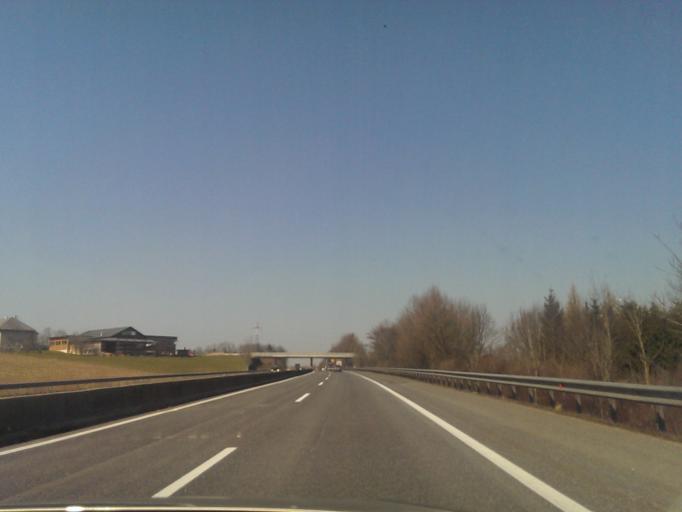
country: AT
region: Upper Austria
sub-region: Politischer Bezirk Kirchdorf an der Krems
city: Kremsmunster
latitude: 47.9952
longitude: 14.0862
